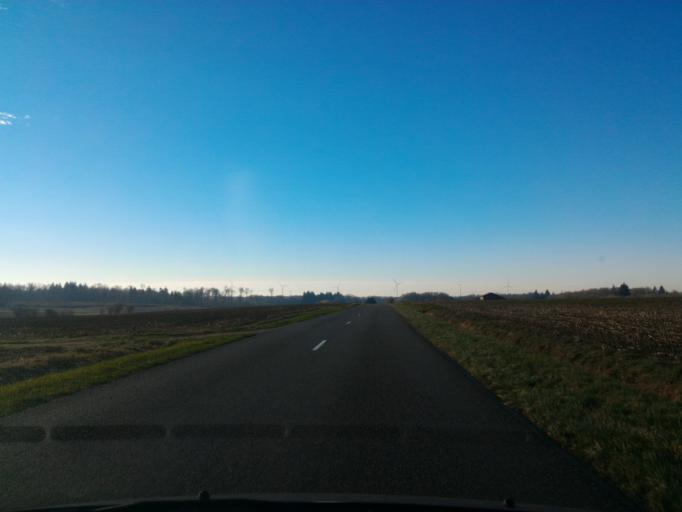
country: FR
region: Poitou-Charentes
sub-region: Departement de la Charente
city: Champagne-Mouton
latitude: 46.0093
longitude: 0.4861
